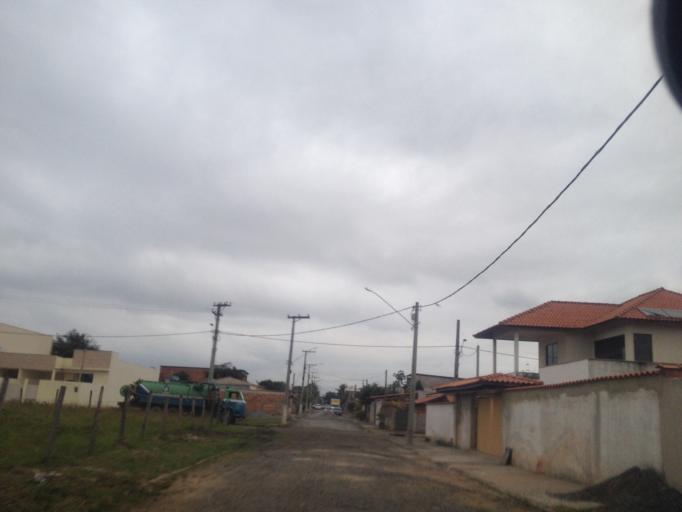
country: BR
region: Rio de Janeiro
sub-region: Porto Real
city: Porto Real
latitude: -22.4076
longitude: -44.2964
